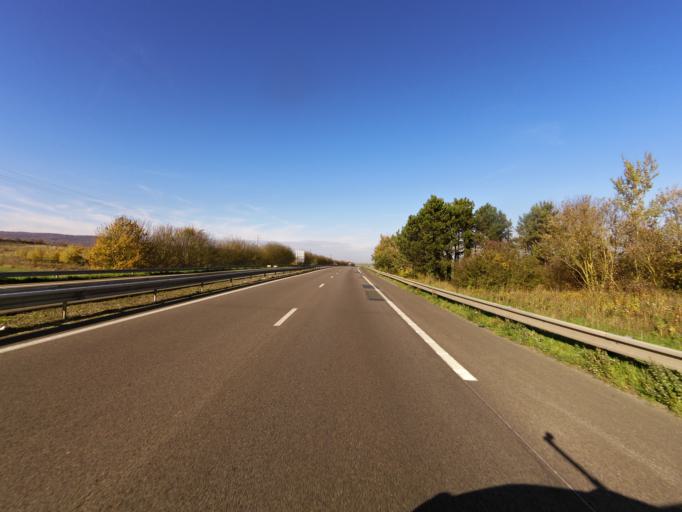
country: FR
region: Champagne-Ardenne
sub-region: Departement de la Marne
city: Verzy
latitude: 49.1284
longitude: 4.2292
